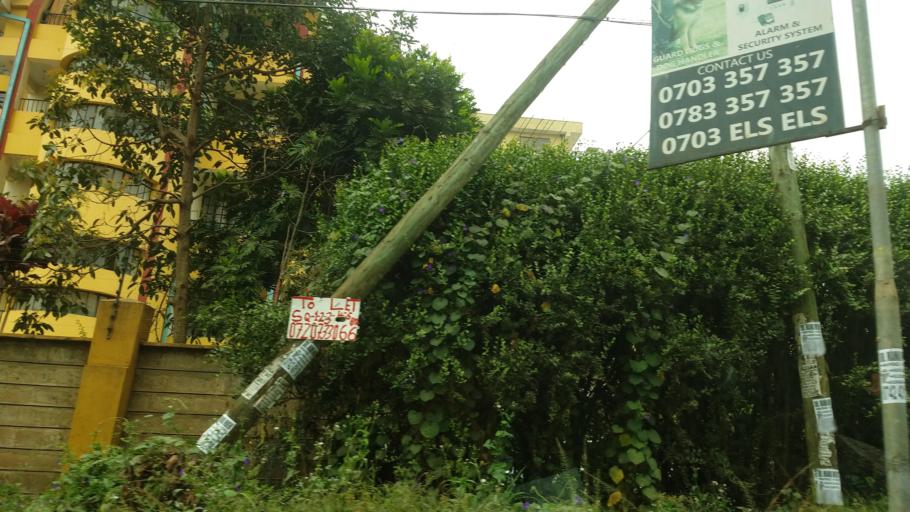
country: KE
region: Nairobi Area
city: Nairobi
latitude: -1.2992
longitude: 36.7820
